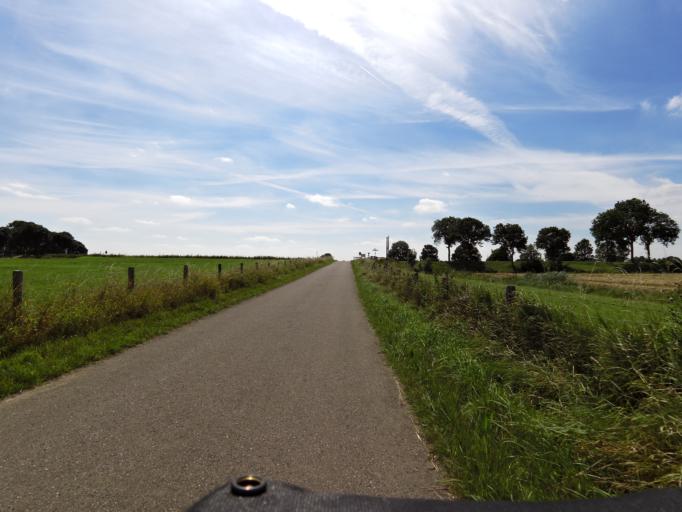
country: NL
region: South Holland
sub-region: Gemeente Binnenmaas
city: Heinenoord
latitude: 51.8491
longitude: 4.4699
